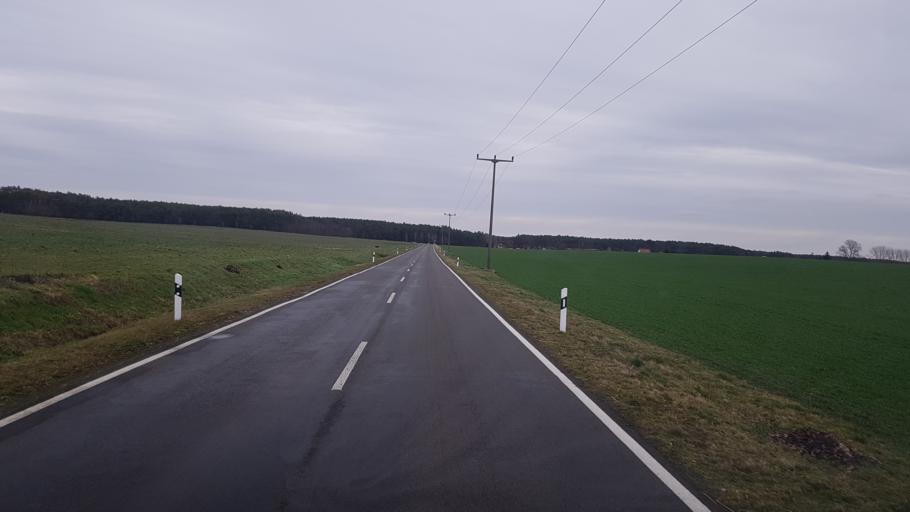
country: DE
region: Brandenburg
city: Crinitz
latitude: 51.7076
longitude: 13.7099
